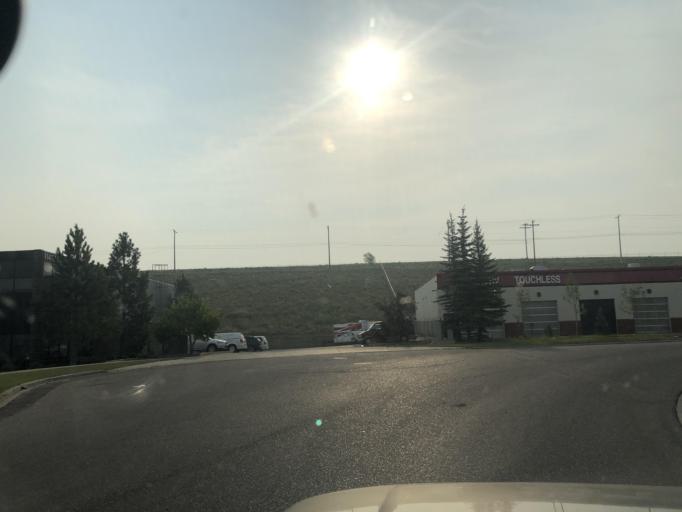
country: CA
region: Alberta
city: Calgary
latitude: 50.9529
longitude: -113.9952
